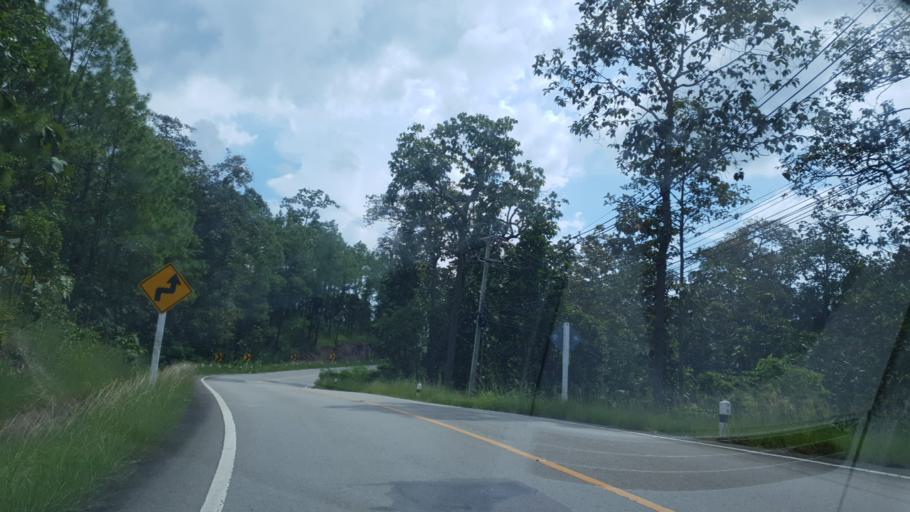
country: TH
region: Mae Hong Son
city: Khun Yuam
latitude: 18.7747
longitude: 97.9404
